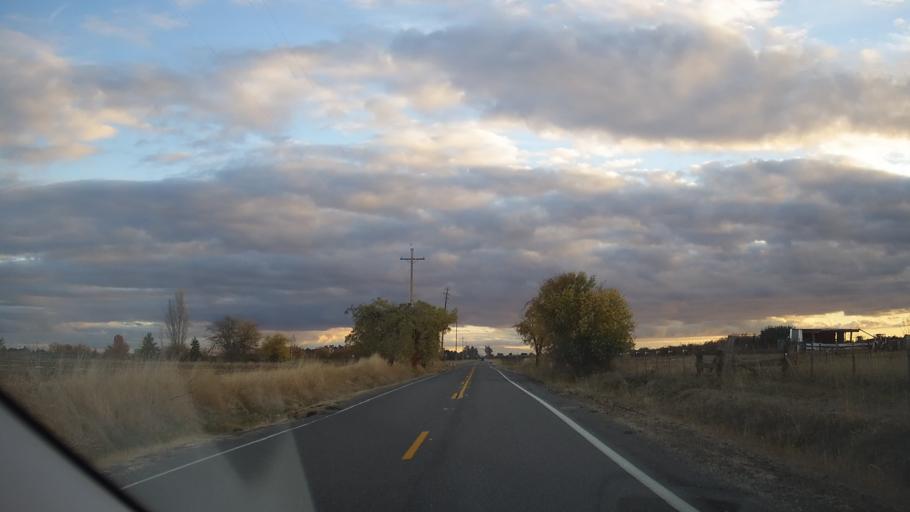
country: US
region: California
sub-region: Solano County
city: Hartley
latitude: 38.3967
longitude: -121.9059
